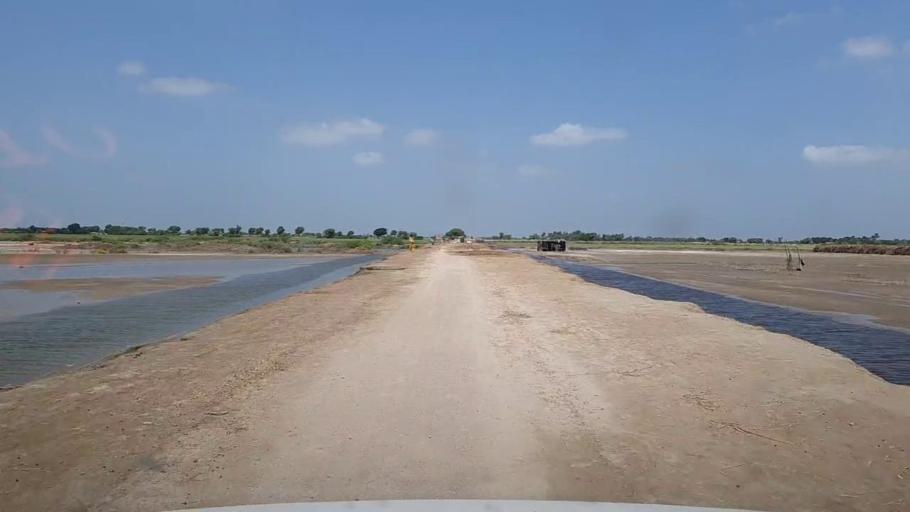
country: PK
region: Sindh
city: Kario
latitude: 24.6968
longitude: 68.5861
